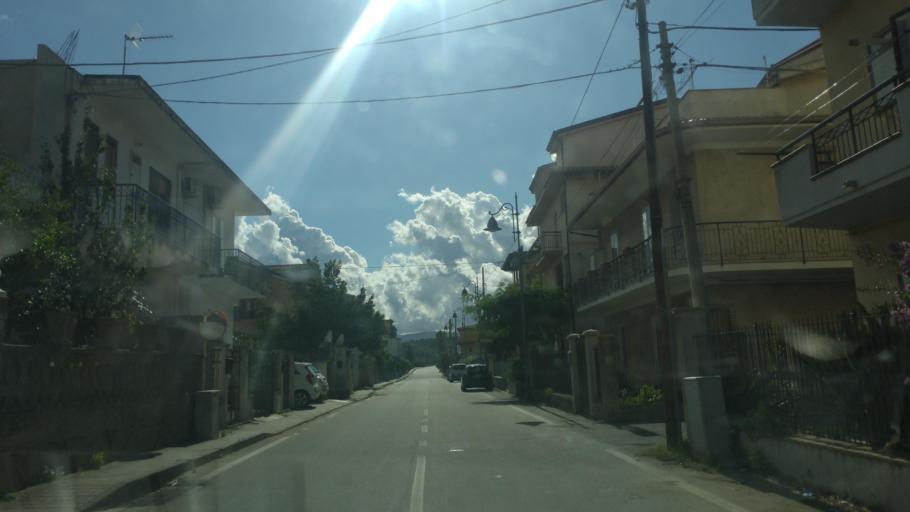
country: IT
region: Calabria
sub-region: Provincia di Catanzaro
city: Staletti
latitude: 38.7655
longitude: 16.5373
